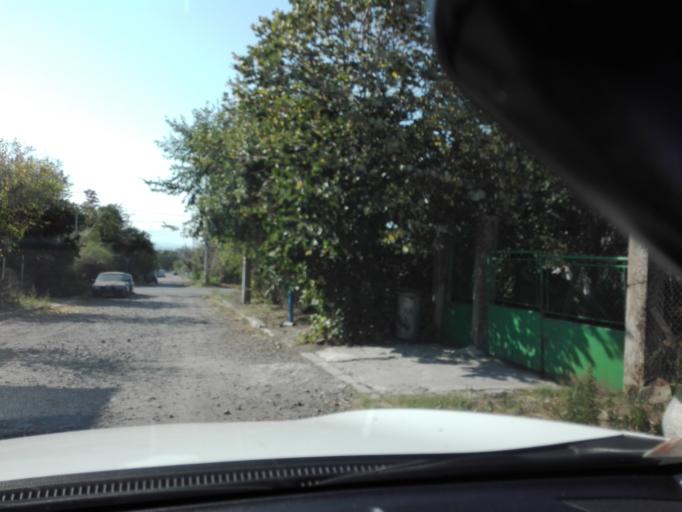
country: BG
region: Burgas
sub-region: Obshtina Kameno
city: Kameno
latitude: 42.6285
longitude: 27.3866
